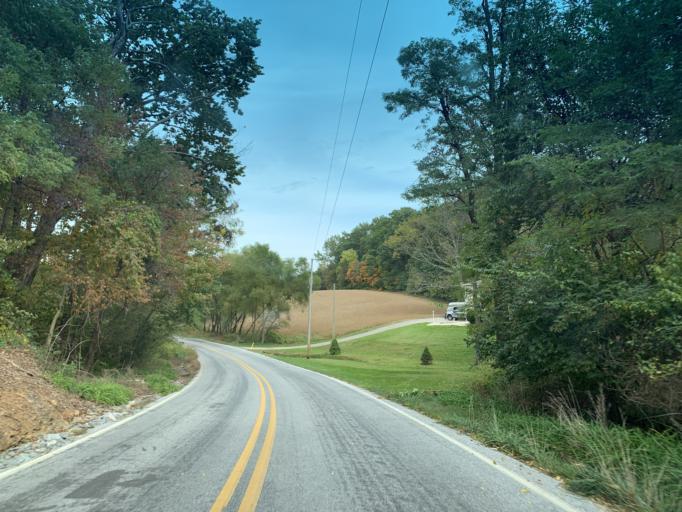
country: US
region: Pennsylvania
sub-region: York County
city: Stewartstown
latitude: 39.8137
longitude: -76.5214
